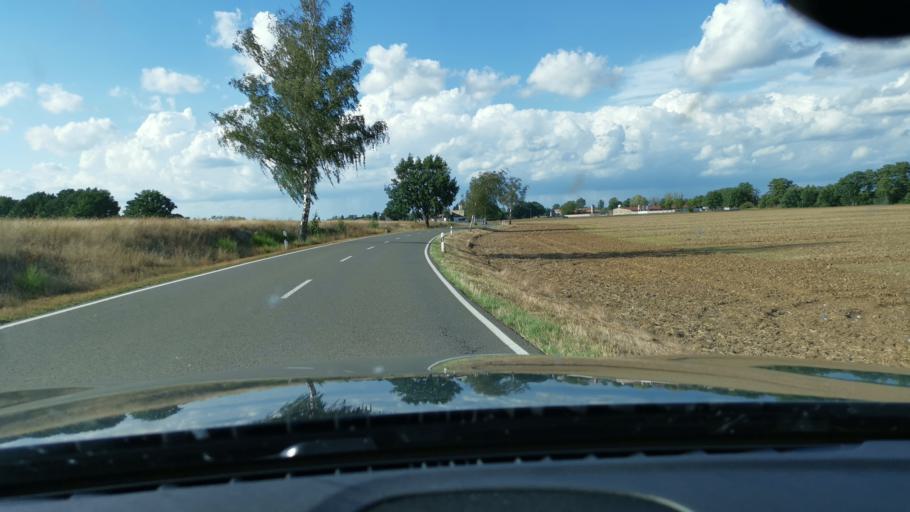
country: DE
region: Saxony
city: Bad Duben
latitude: 51.5507
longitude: 12.5769
